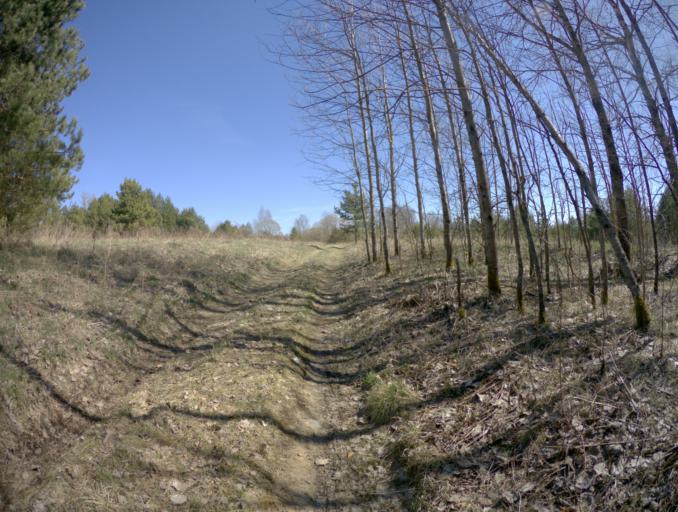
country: RU
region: Vladimir
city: Ivanishchi
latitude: 55.8626
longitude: 40.4288
